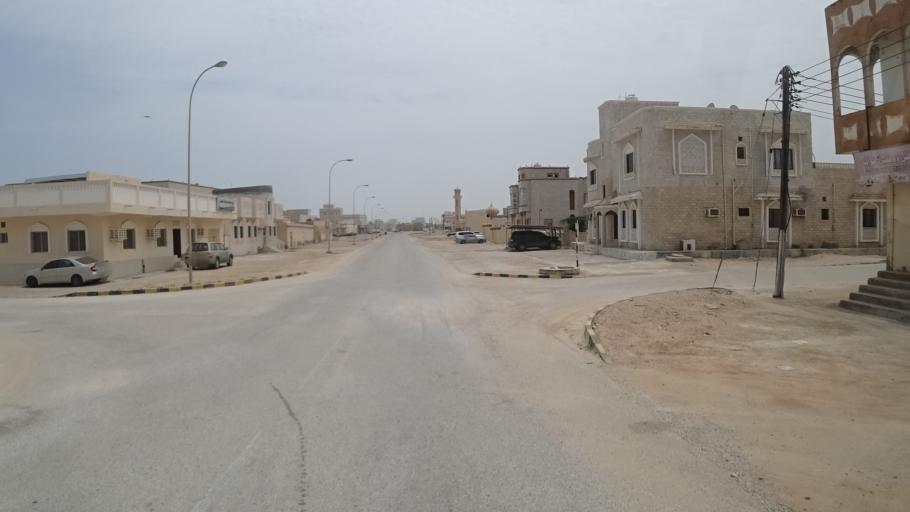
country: OM
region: Zufar
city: Salalah
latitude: 17.0370
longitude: 54.4067
